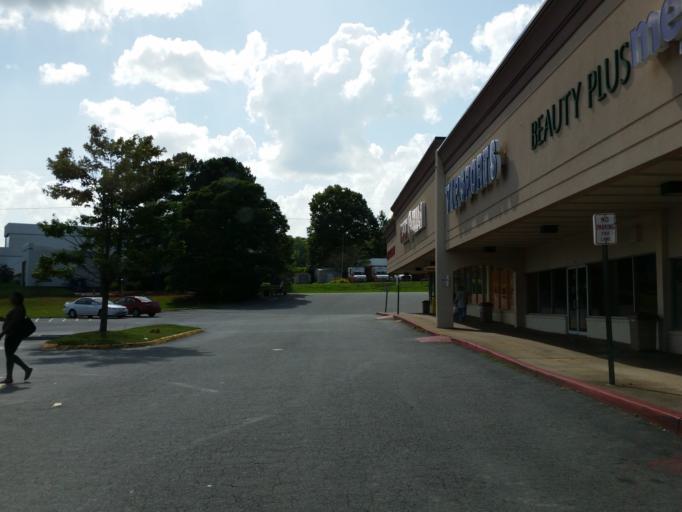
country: US
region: Georgia
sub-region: Cobb County
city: Marietta
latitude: 33.9444
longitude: -84.5330
